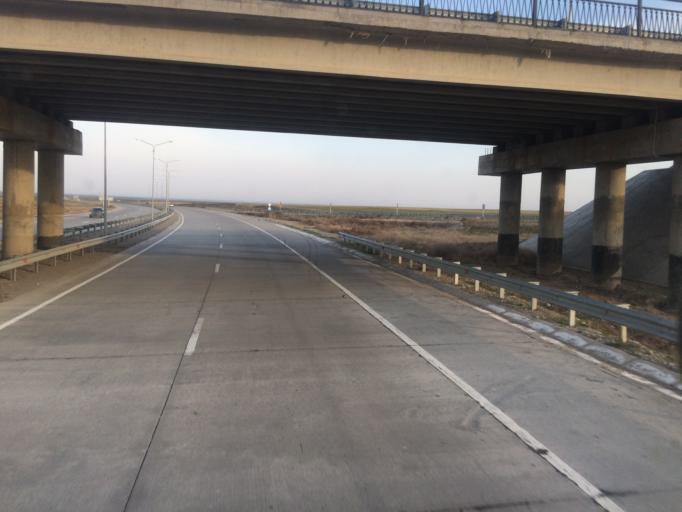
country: KZ
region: Ongtustik Qazaqstan
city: Temirlanovka
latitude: 42.6491
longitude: 69.2388
